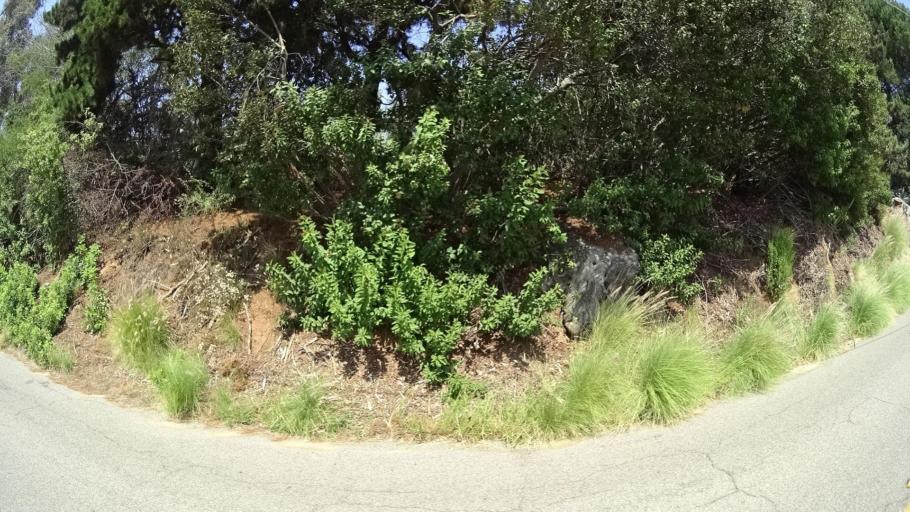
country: US
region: California
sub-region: San Diego County
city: Bonsall
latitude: 33.3138
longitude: -117.2294
